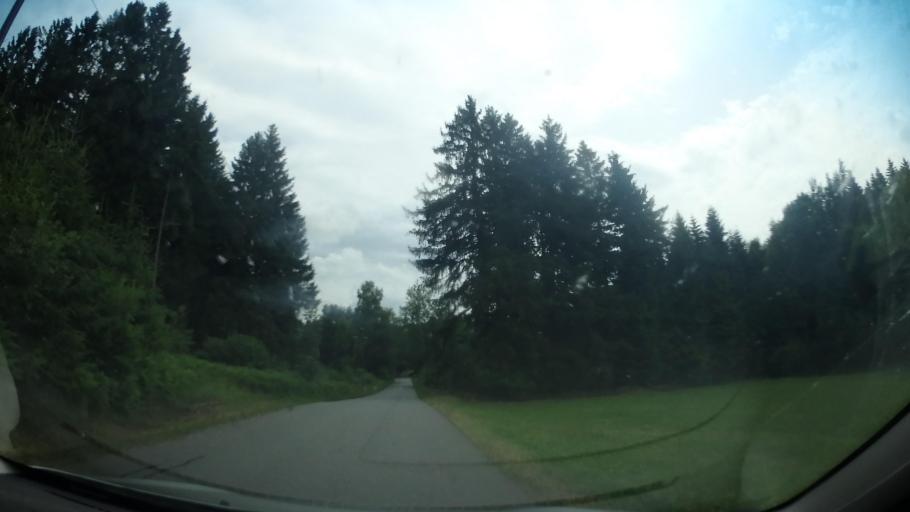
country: CZ
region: Vysocina
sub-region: Okres Zd'ar nad Sazavou
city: Nove Mesto na Morave
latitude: 49.6020
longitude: 16.0507
